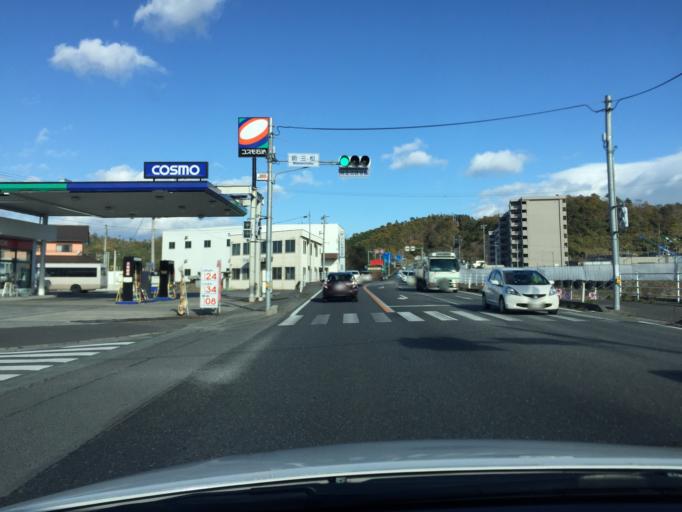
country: JP
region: Fukushima
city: Iwaki
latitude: 37.1459
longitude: 140.9959
